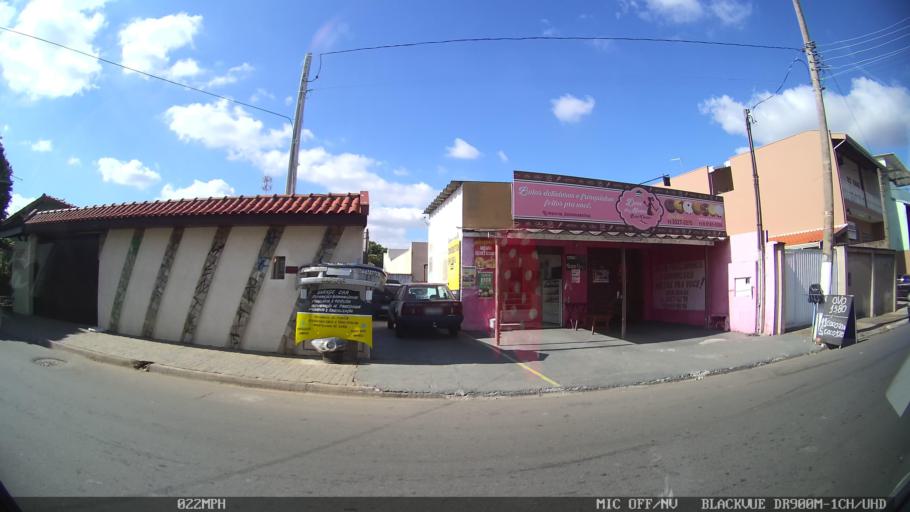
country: BR
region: Sao Paulo
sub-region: Hortolandia
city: Hortolandia
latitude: -22.8838
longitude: -47.2021
